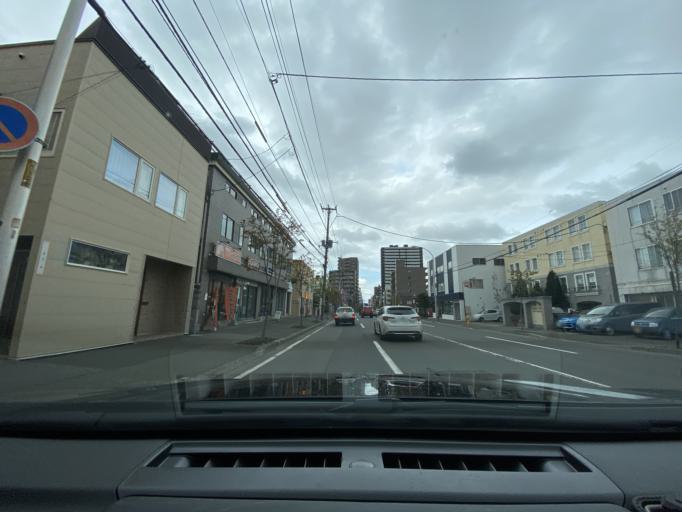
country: JP
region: Hokkaido
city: Sapporo
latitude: 43.0707
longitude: 141.2971
